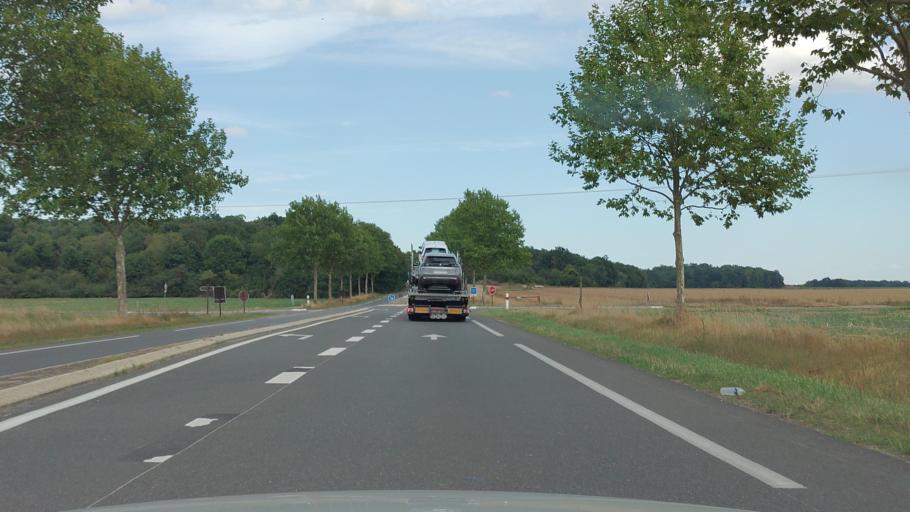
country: FR
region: Ile-de-France
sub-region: Departement de Seine-et-Marne
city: Maincy
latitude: 48.5423
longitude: 2.7026
